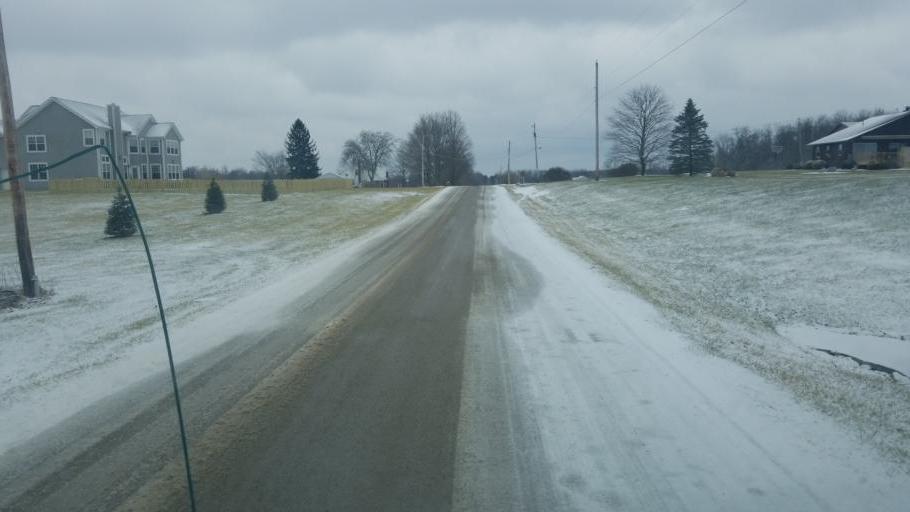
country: US
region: Ohio
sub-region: Delaware County
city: Sunbury
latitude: 40.3701
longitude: -82.8162
